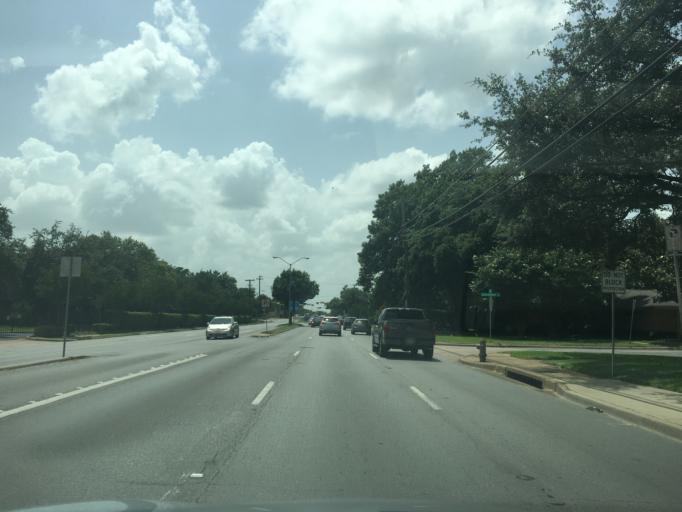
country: US
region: Texas
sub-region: Dallas County
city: University Park
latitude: 32.8949
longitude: -96.8068
